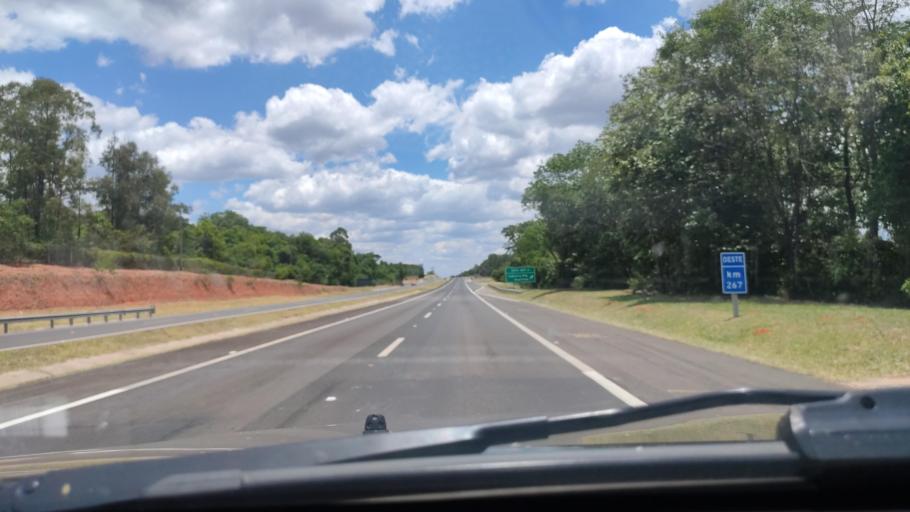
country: BR
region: Sao Paulo
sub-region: Duartina
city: Duartina
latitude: -22.5098
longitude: -49.2986
